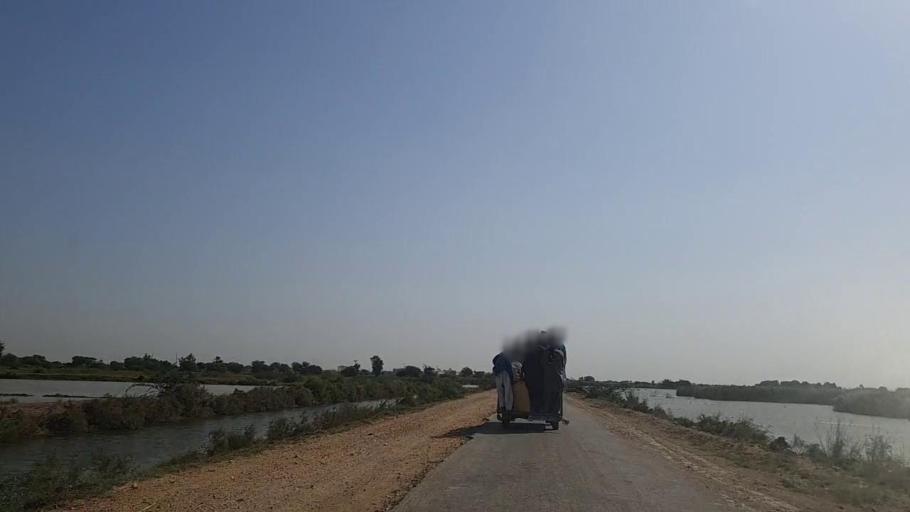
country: PK
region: Sindh
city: Mirpur Batoro
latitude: 24.6501
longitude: 68.2886
